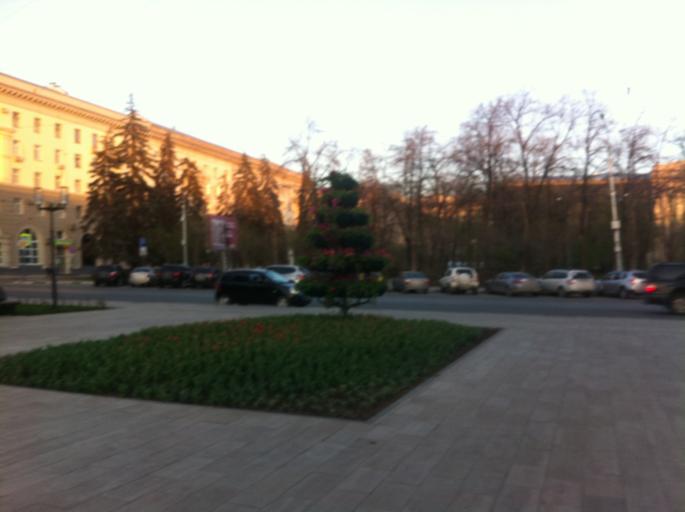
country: RU
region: Samara
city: Samara
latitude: 53.2018
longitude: 50.1123
